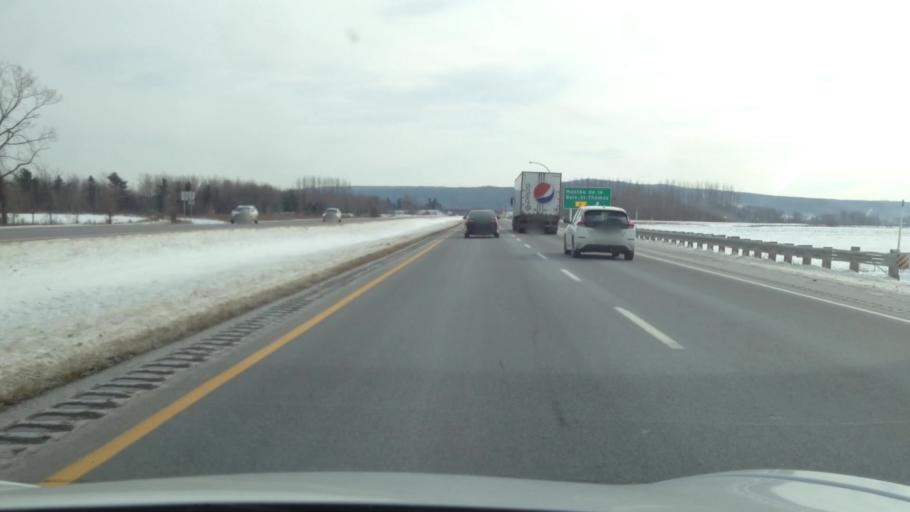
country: CA
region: Quebec
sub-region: Monteregie
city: Rigaud
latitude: 45.4987
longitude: -74.3571
